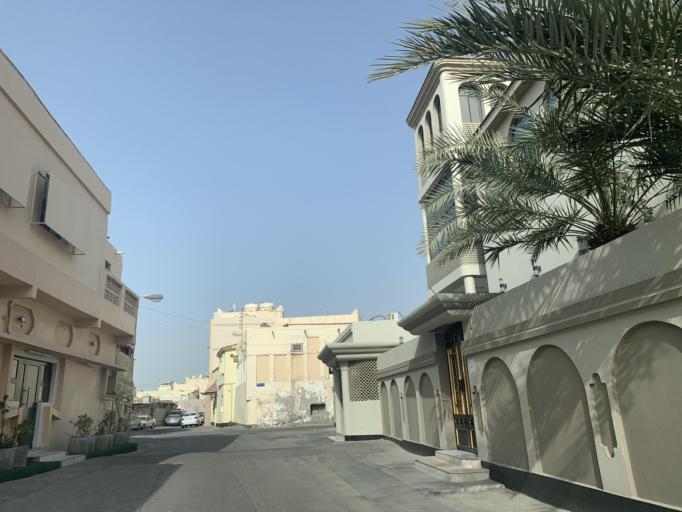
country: BH
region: Northern
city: Madinat `Isa
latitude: 26.1628
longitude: 50.5157
